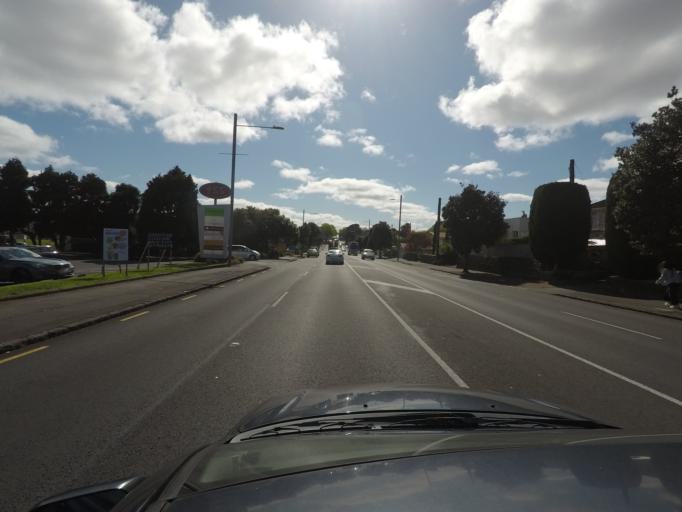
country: NZ
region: Auckland
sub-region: Auckland
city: Rosebank
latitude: -36.8877
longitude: 174.7118
